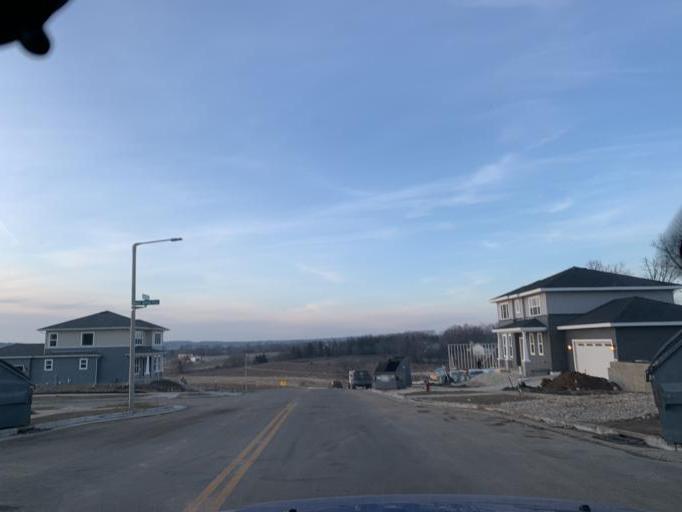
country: US
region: Wisconsin
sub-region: Dane County
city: Verona
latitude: 43.0474
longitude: -89.5589
